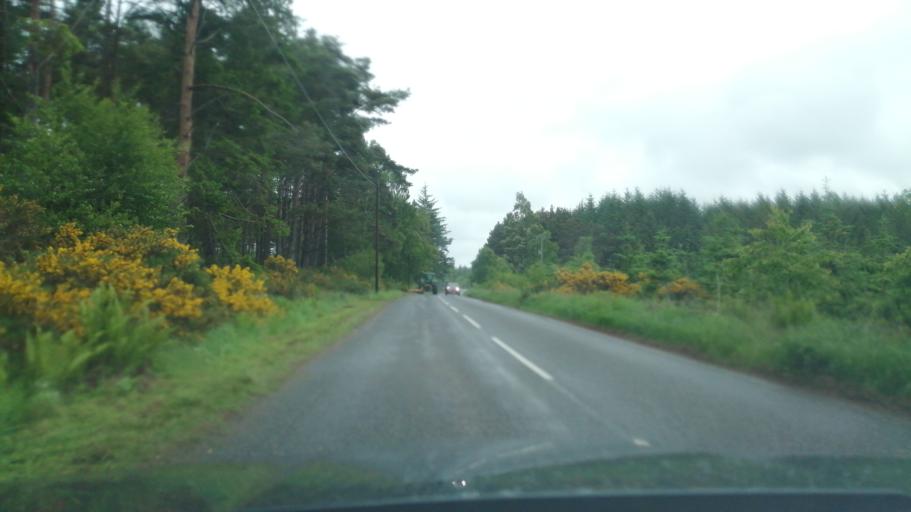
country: GB
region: Scotland
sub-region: Aberdeenshire
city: Portsoy
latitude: 57.6257
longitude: -2.7203
